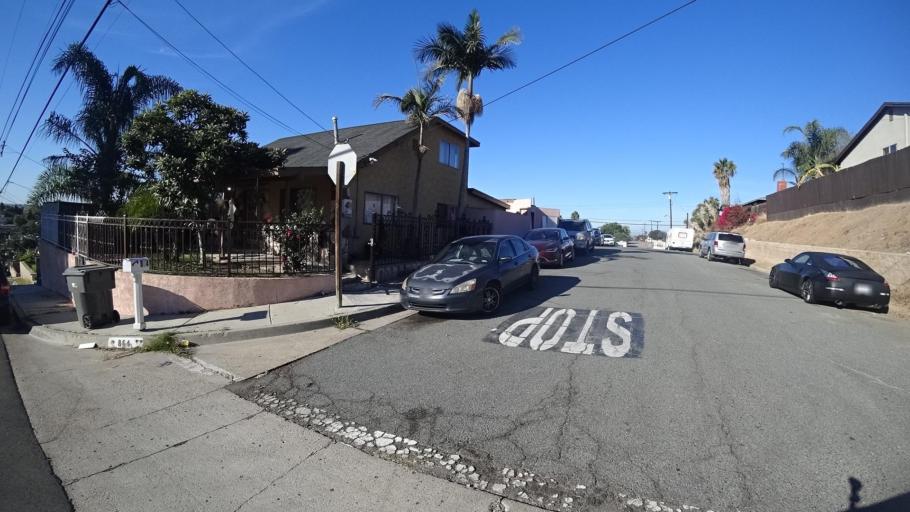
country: US
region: California
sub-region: San Diego County
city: La Presa
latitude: 32.7134
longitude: -116.9924
